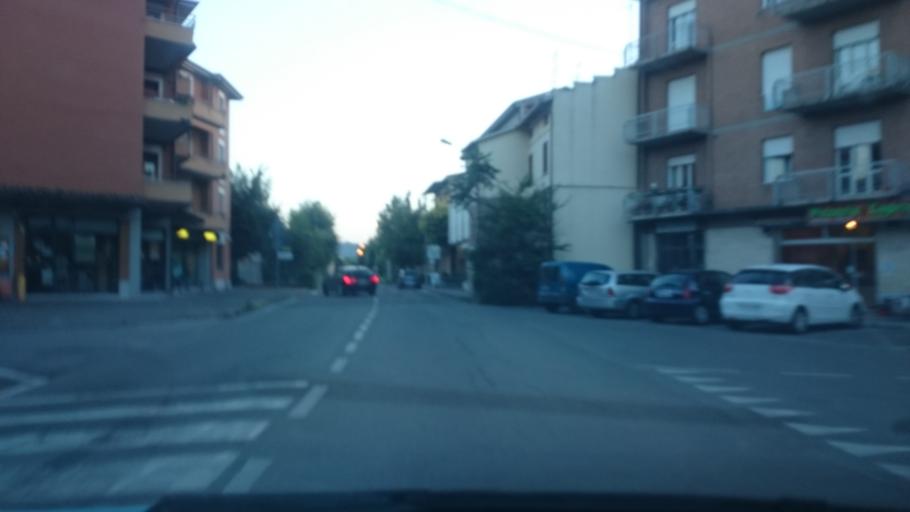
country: IT
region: Emilia-Romagna
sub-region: Provincia di Reggio Emilia
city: Arceto
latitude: 44.6194
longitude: 10.7217
